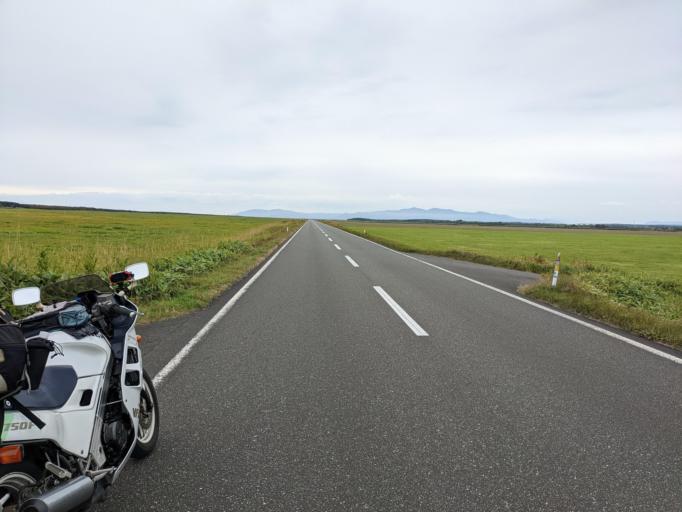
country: JP
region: Hokkaido
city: Makubetsu
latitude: 45.2317
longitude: 142.2684
